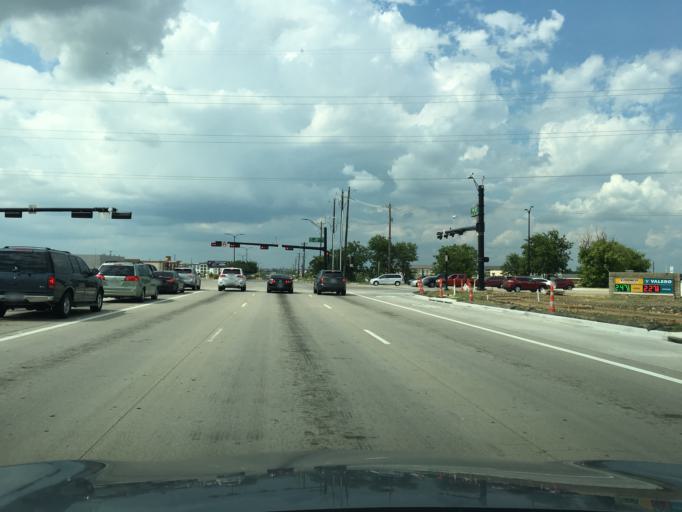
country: US
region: Texas
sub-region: Denton County
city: Little Elm
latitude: 33.1529
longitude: -96.8908
